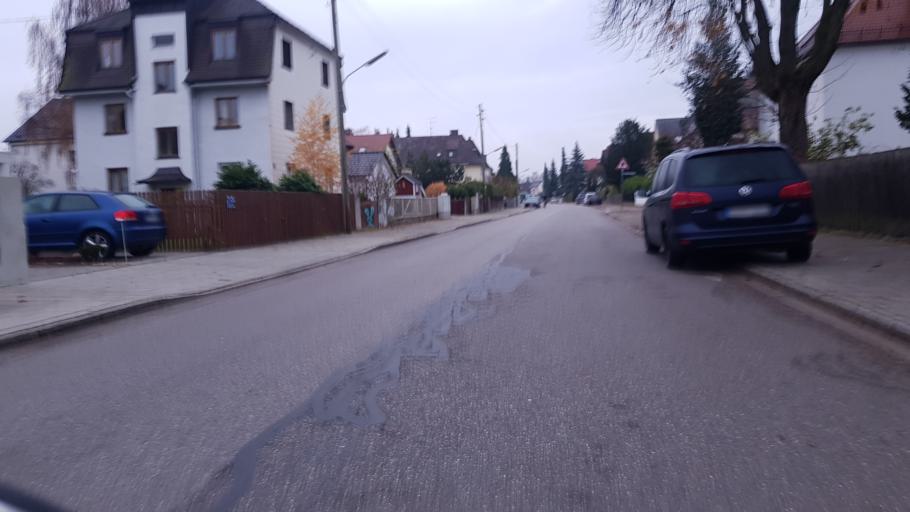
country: DE
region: Bavaria
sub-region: Upper Bavaria
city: Bogenhausen
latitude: 48.1150
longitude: 11.6257
